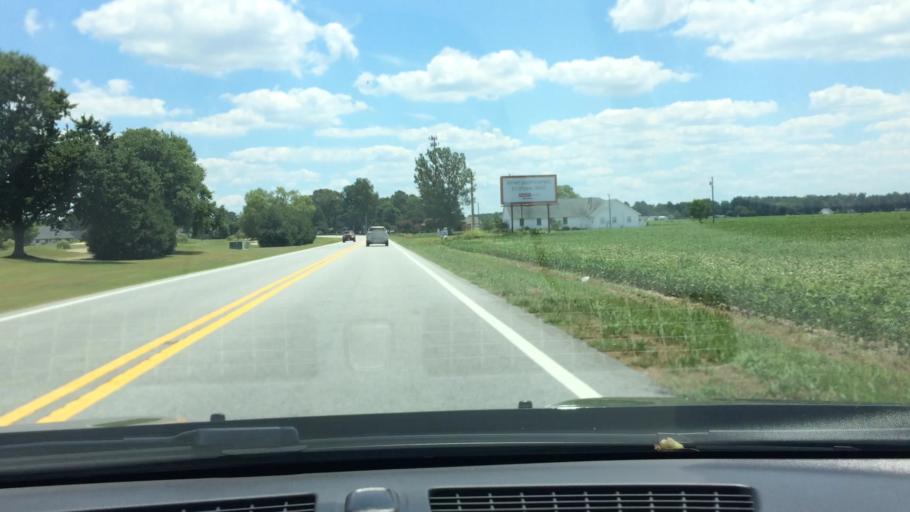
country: US
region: North Carolina
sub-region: Pitt County
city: Summerfield
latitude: 35.6374
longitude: -77.4510
